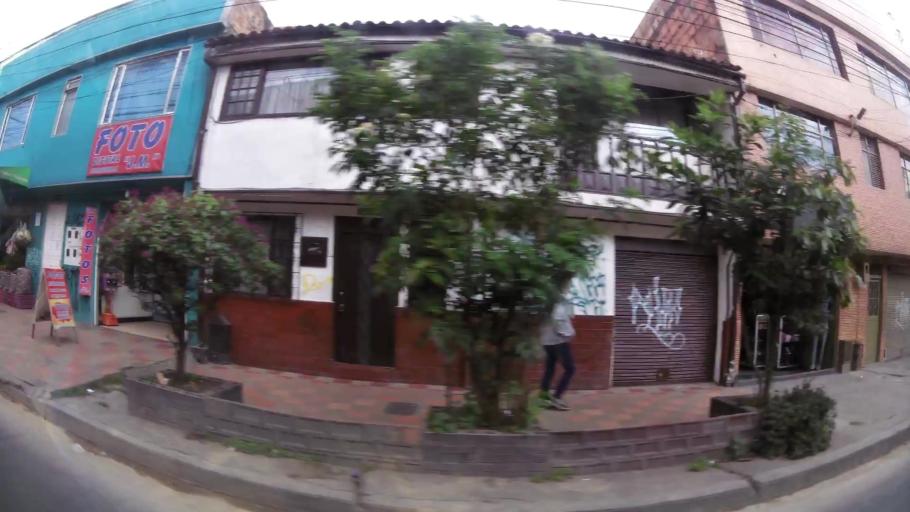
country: CO
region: Bogota D.C.
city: Bogota
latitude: 4.5555
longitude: -74.1123
